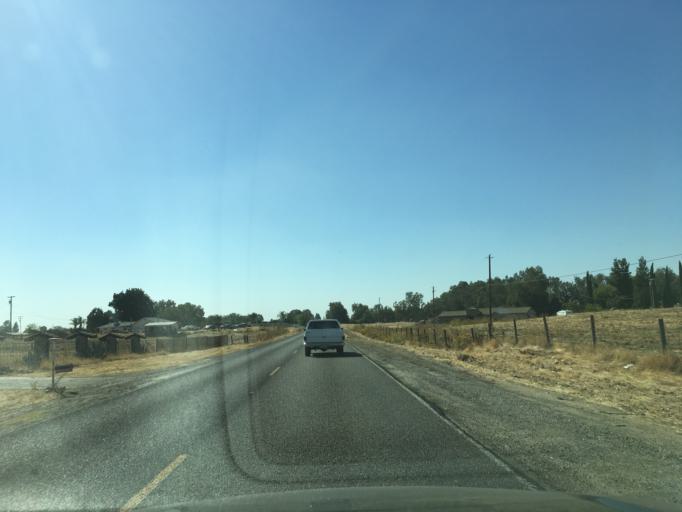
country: US
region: California
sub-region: Madera County
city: Parksdale
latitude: 36.9982
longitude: -119.9803
